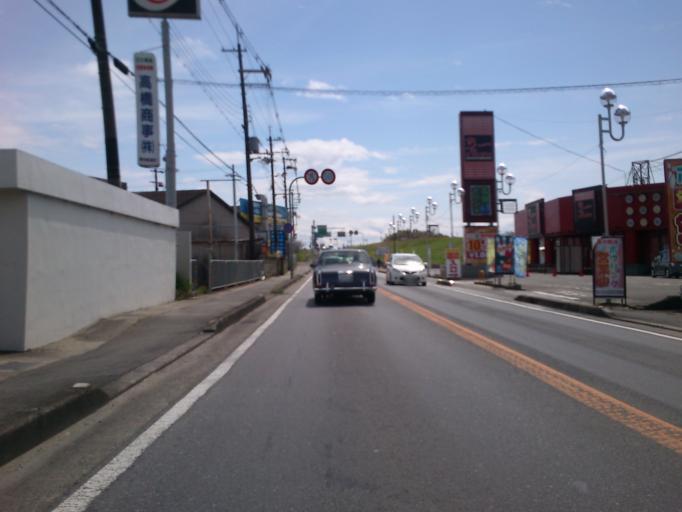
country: JP
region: Kyoto
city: Tanabe
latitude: 34.8262
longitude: 135.7938
